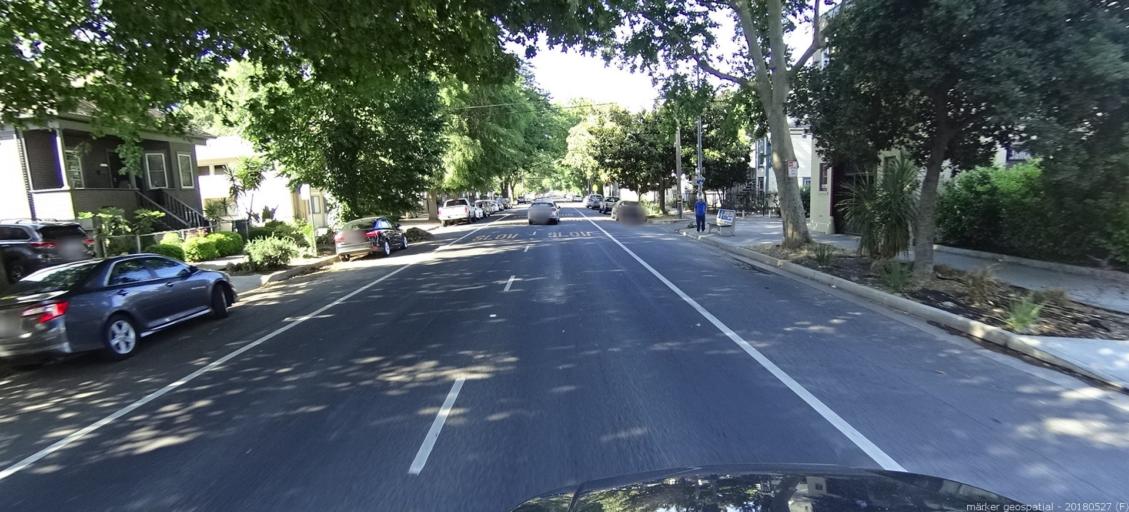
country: US
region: California
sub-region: Sacramento County
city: Sacramento
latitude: 38.5695
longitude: -121.4997
